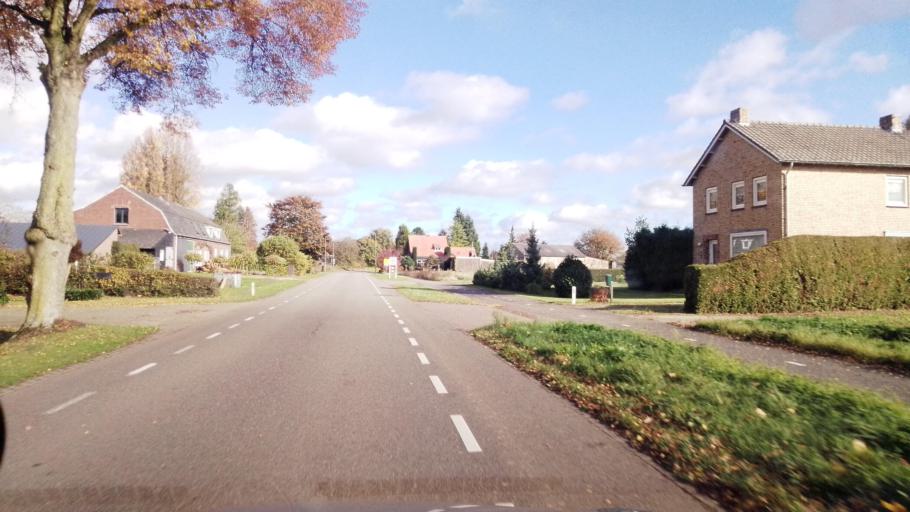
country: NL
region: Limburg
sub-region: Gemeente Venlo
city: Arcen
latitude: 51.4772
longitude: 6.1485
